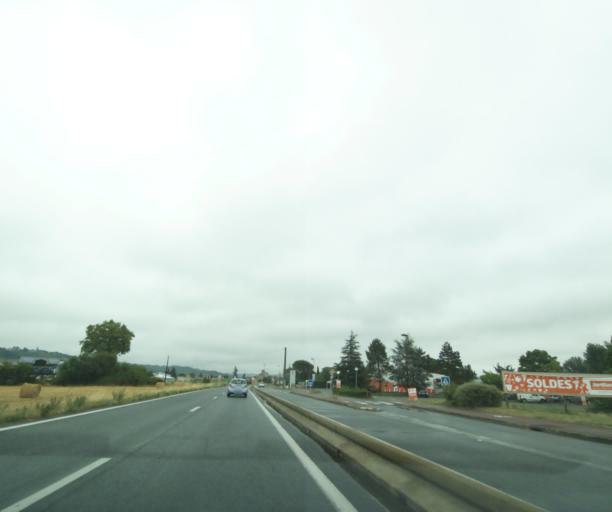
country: FR
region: Midi-Pyrenees
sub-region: Departement du Tarn
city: Albi
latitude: 43.9567
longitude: 2.1582
